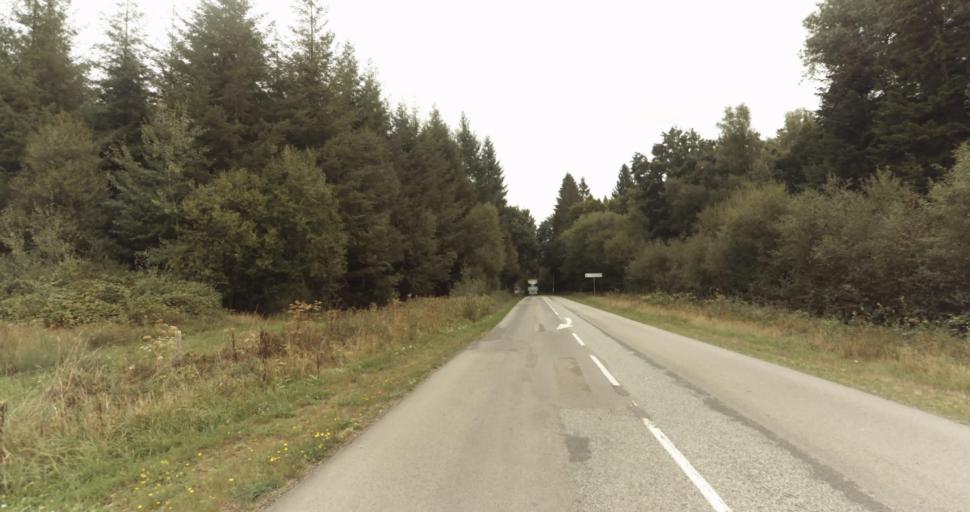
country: FR
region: Lower Normandy
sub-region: Departement de l'Orne
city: Gace
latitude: 48.7954
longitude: 0.3391
